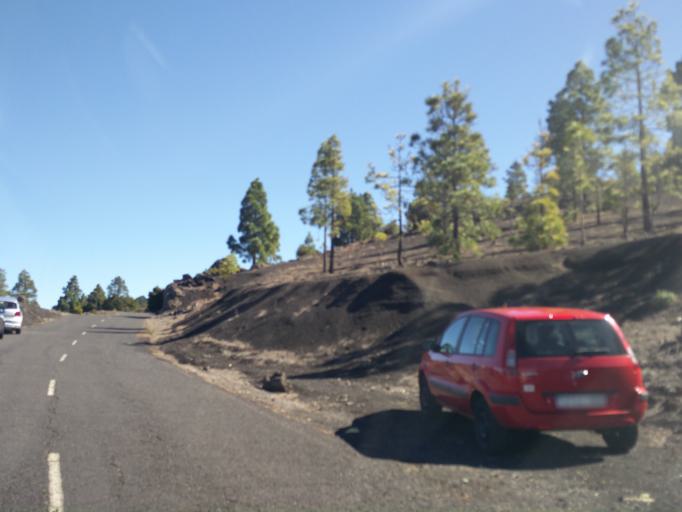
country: ES
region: Canary Islands
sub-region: Provincia de Santa Cruz de Tenerife
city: El Paso
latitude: 28.6173
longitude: -17.8481
